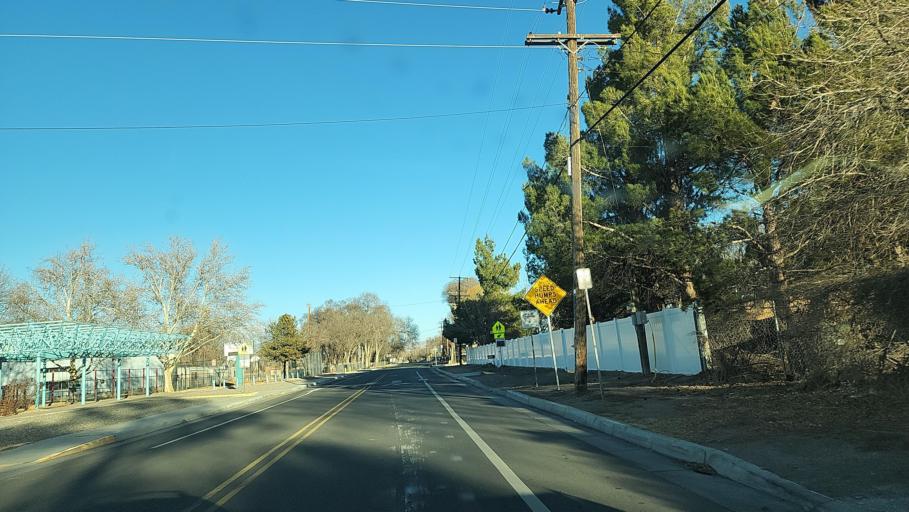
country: US
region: New Mexico
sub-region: Bernalillo County
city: South Valley
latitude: 35.0306
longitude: -106.6936
